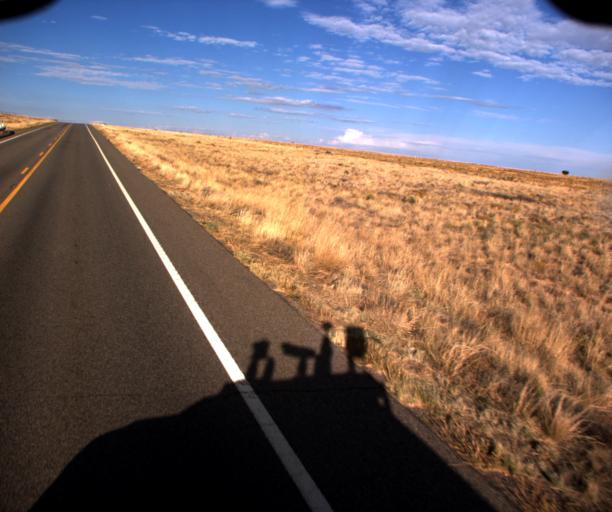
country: US
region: Arizona
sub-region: Apache County
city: Lukachukai
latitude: 36.9271
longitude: -109.1866
